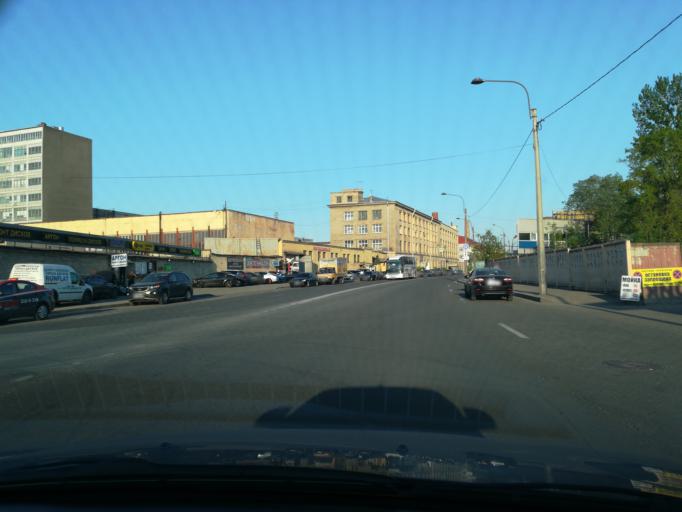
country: RU
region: St.-Petersburg
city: Vasyl'evsky Ostrov
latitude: 59.9559
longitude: 30.2514
